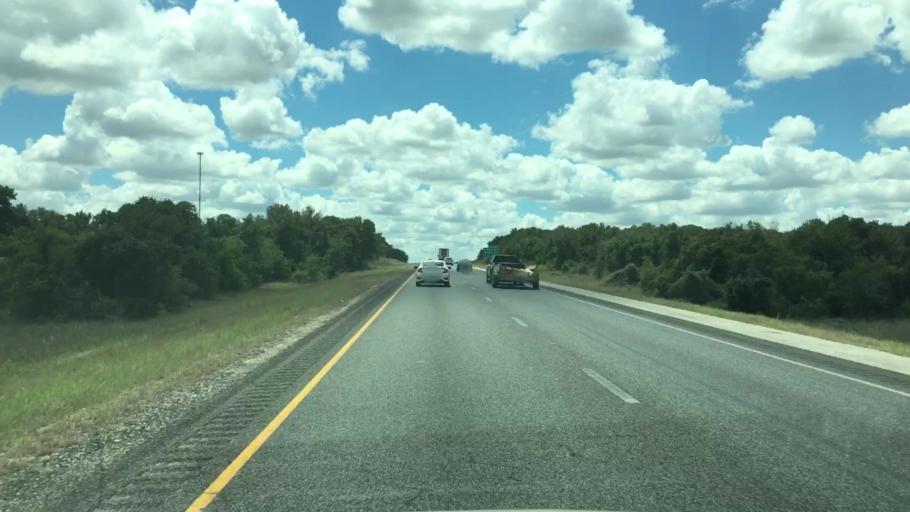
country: US
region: Texas
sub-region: Bexar County
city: Elmendorf
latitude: 29.1923
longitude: -98.4230
